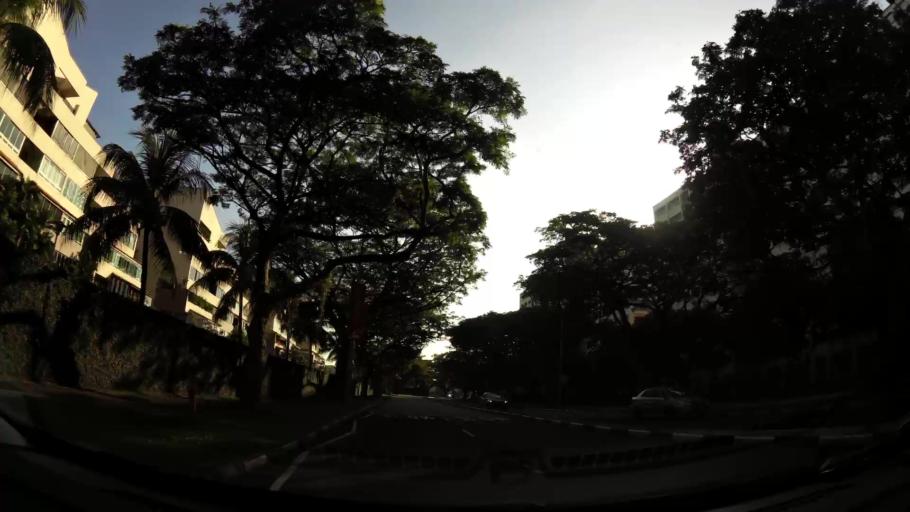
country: SG
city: Singapore
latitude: 1.3210
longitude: 103.9444
